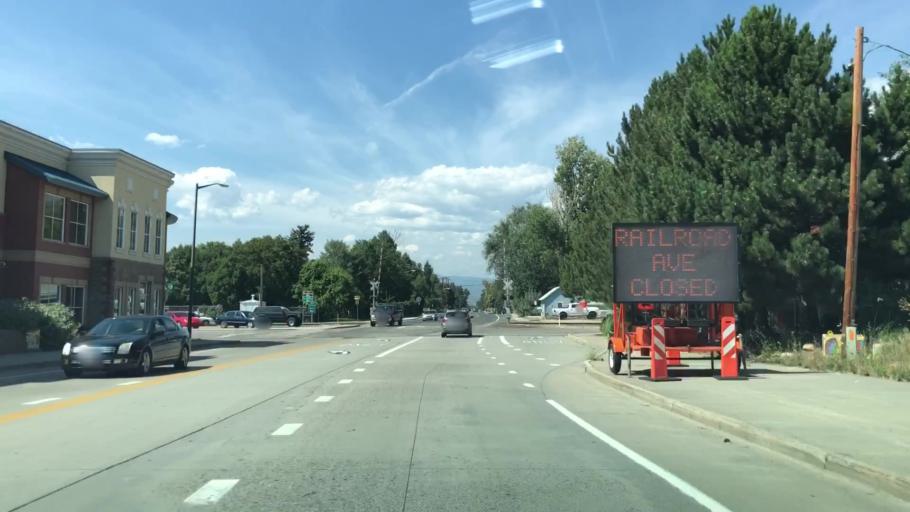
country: US
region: Colorado
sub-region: Larimer County
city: Loveland
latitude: 40.3927
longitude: -105.0753
